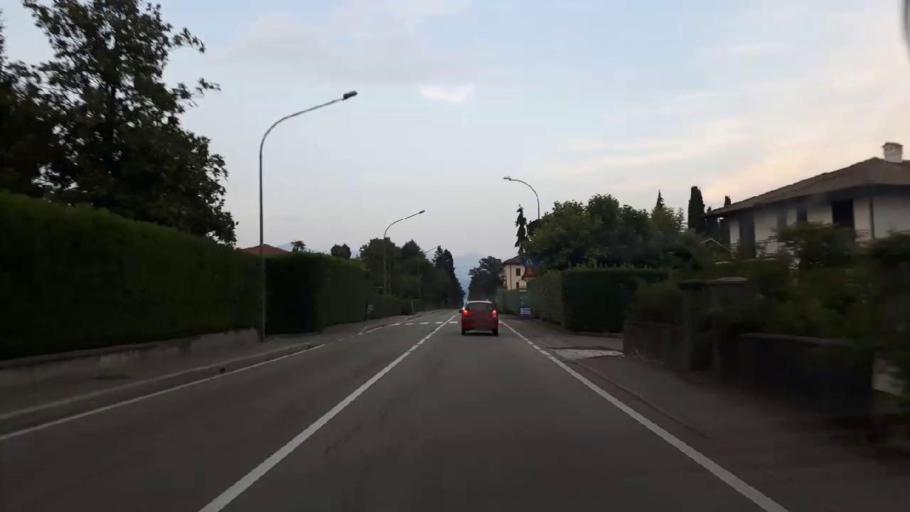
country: IT
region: Piedmont
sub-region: Provincia di Novara
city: Lesa
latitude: 45.8244
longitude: 8.5607
